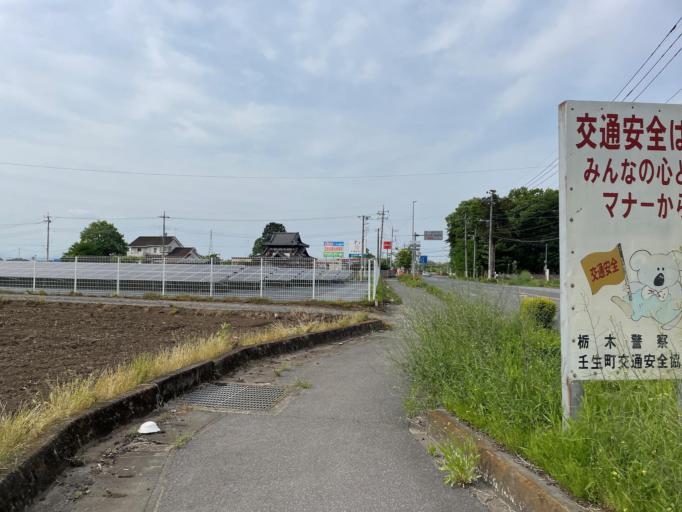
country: JP
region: Tochigi
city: Mibu
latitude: 36.4036
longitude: 139.8036
